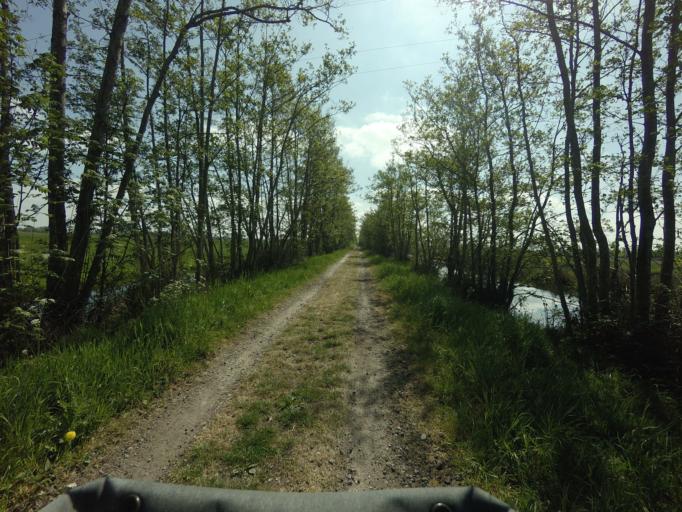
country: NL
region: South Holland
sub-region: Gemeente Gouda
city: Gouda
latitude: 51.9902
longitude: 4.7132
